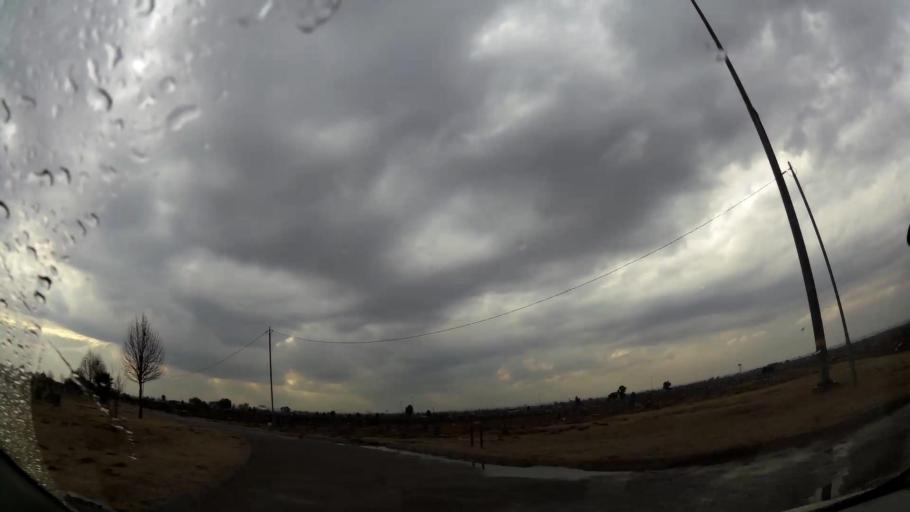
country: ZA
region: Gauteng
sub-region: Ekurhuleni Metropolitan Municipality
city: Germiston
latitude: -26.3778
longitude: 28.1400
